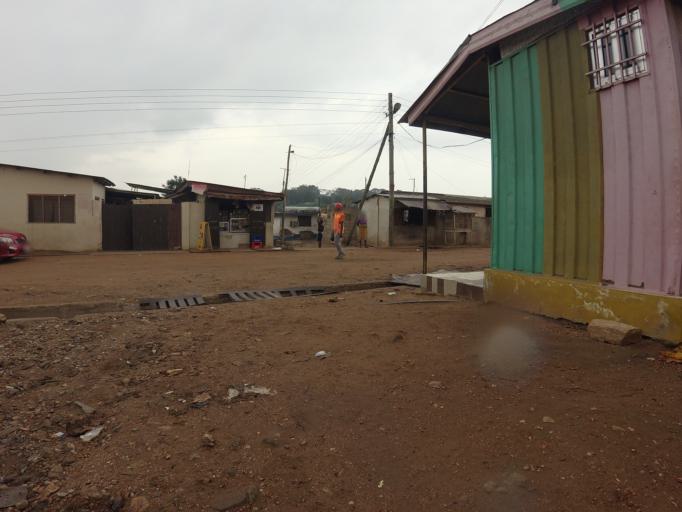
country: GH
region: Greater Accra
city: Dome
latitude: 5.6288
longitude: -0.2318
